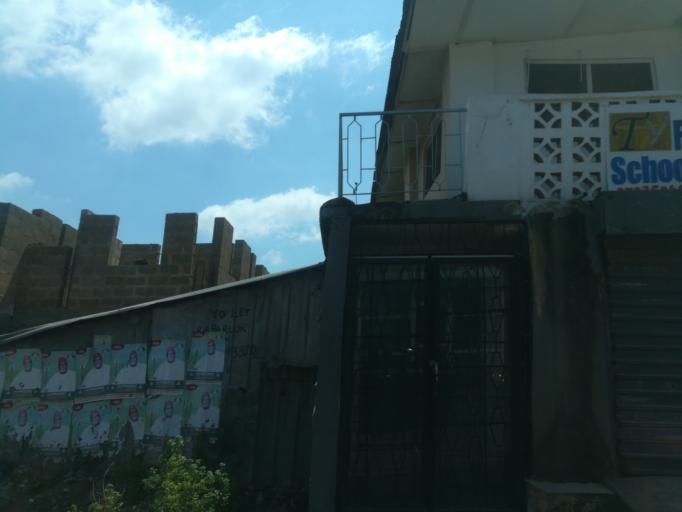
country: NG
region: Oyo
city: Ibadan
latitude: 7.3610
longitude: 3.8716
